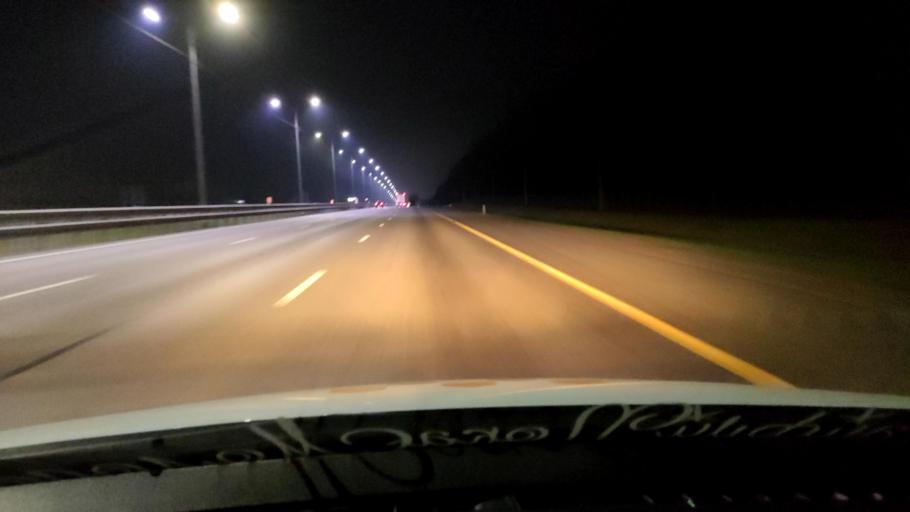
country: RU
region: Voronezj
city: Ramon'
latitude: 51.8823
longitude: 39.2171
